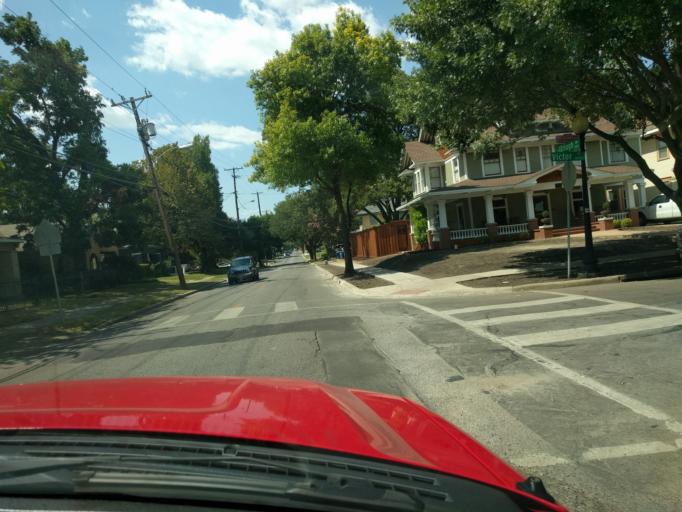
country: US
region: Texas
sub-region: Dallas County
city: Dallas
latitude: 32.7971
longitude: -96.7658
